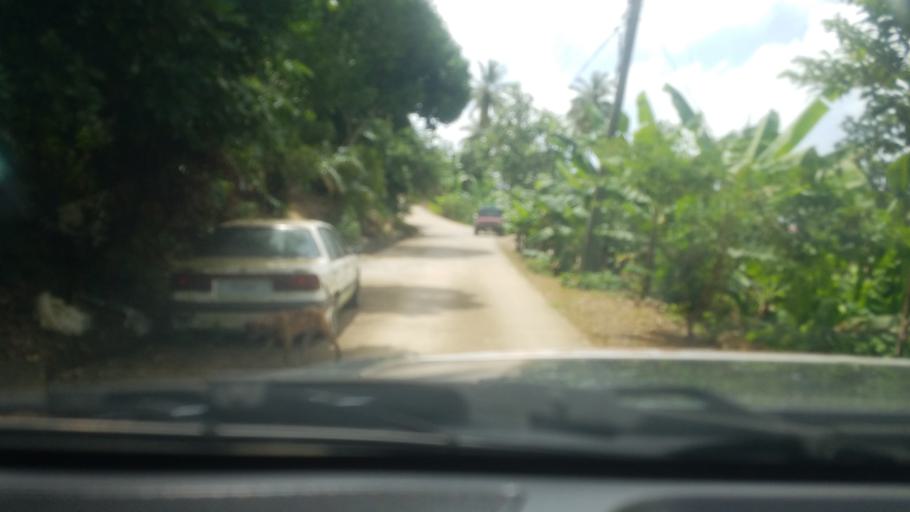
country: LC
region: Micoud Quarter
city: Micoud
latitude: 13.8017
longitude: -60.9502
